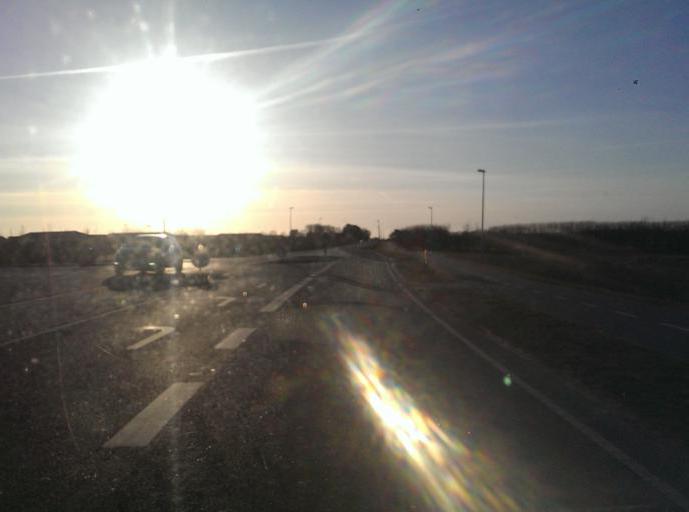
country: DK
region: South Denmark
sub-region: Esbjerg Kommune
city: Esbjerg
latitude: 55.5283
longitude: 8.4292
